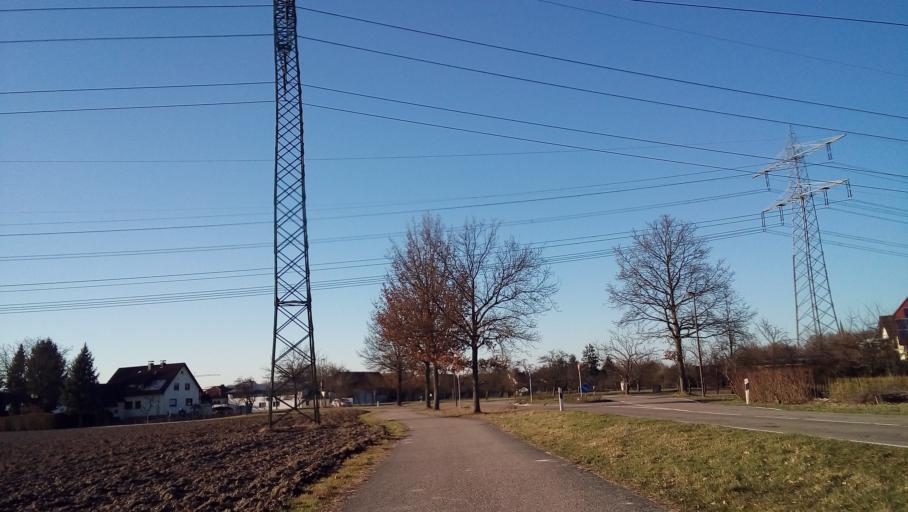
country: DE
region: Baden-Wuerttemberg
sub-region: Freiburg Region
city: Achern
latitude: 48.6475
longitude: 8.0498
